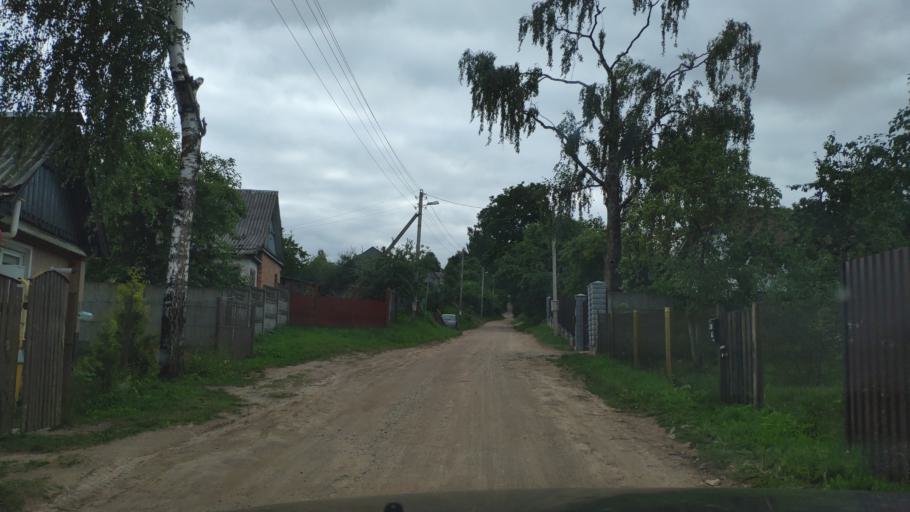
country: BY
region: Minsk
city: Khatsyezhyna
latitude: 53.9263
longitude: 27.2601
